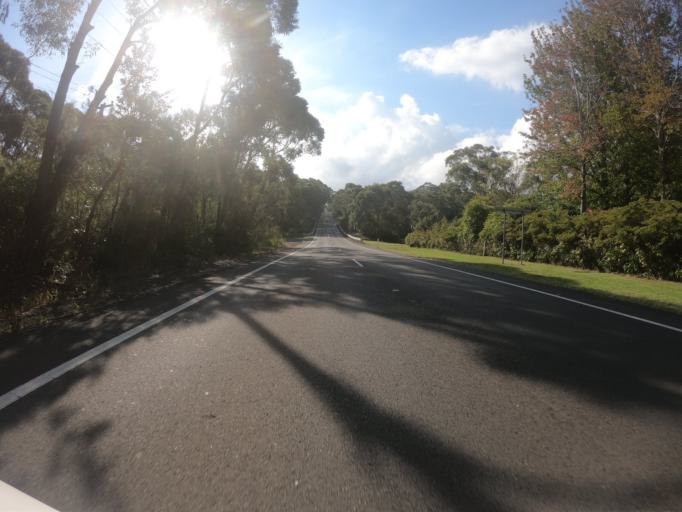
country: AU
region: New South Wales
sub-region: Wollongong
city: Helensburgh
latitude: -34.2141
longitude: 150.9768
